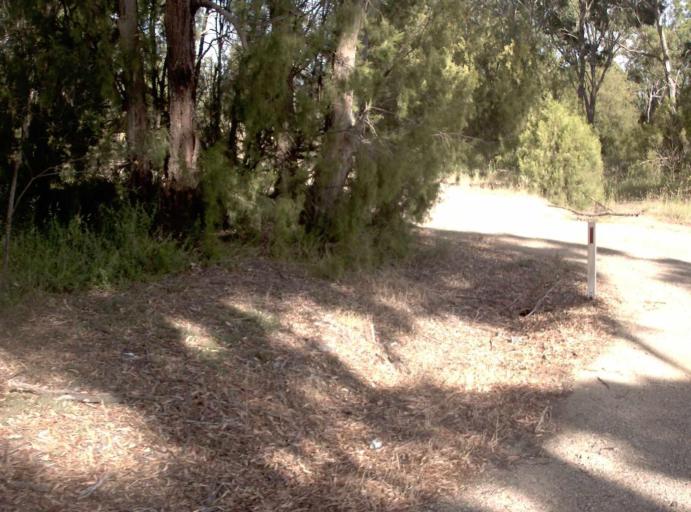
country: AU
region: Victoria
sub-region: East Gippsland
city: Lakes Entrance
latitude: -37.7926
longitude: 147.8309
